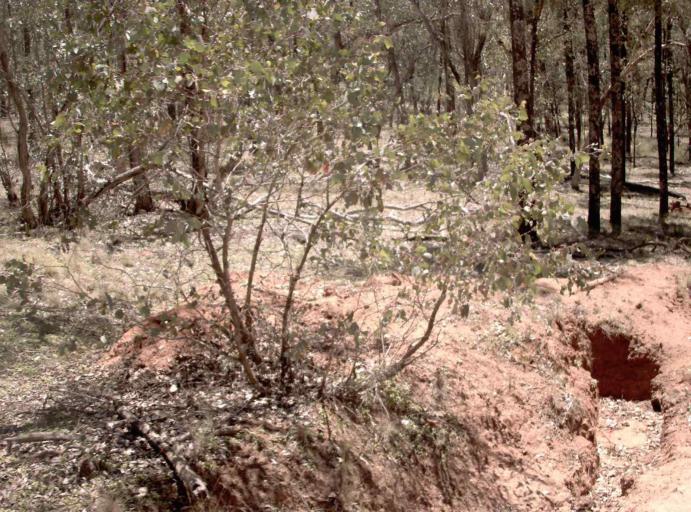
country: AU
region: New South Wales
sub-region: Snowy River
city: Jindabyne
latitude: -36.8965
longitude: 148.4200
